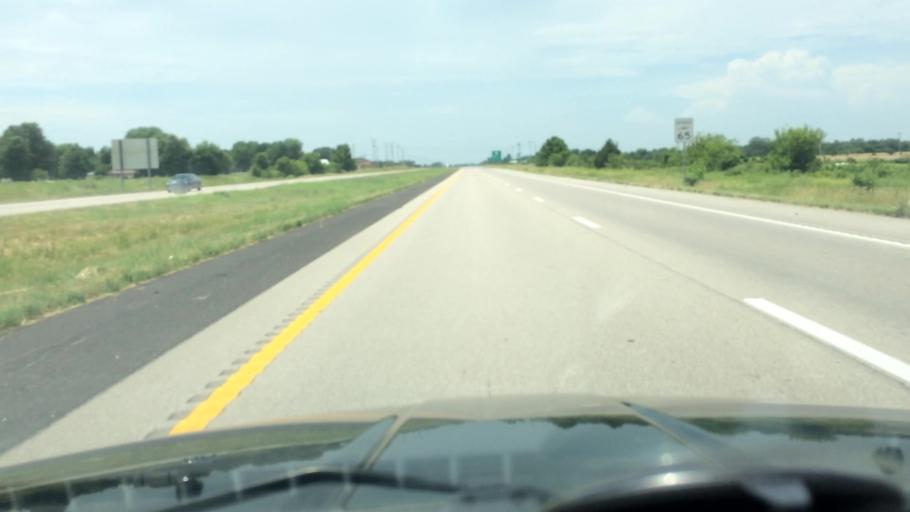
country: US
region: Missouri
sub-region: Polk County
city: Bolivar
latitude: 37.5806
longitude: -93.4070
